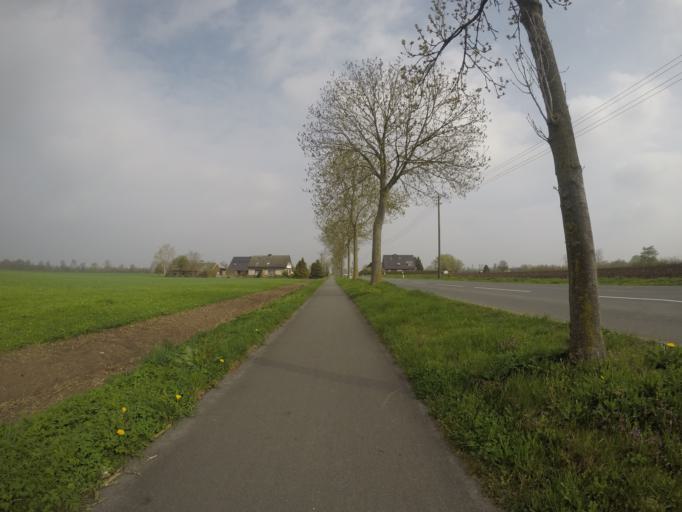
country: DE
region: North Rhine-Westphalia
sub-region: Regierungsbezirk Munster
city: Isselburg
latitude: 51.8430
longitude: 6.5015
